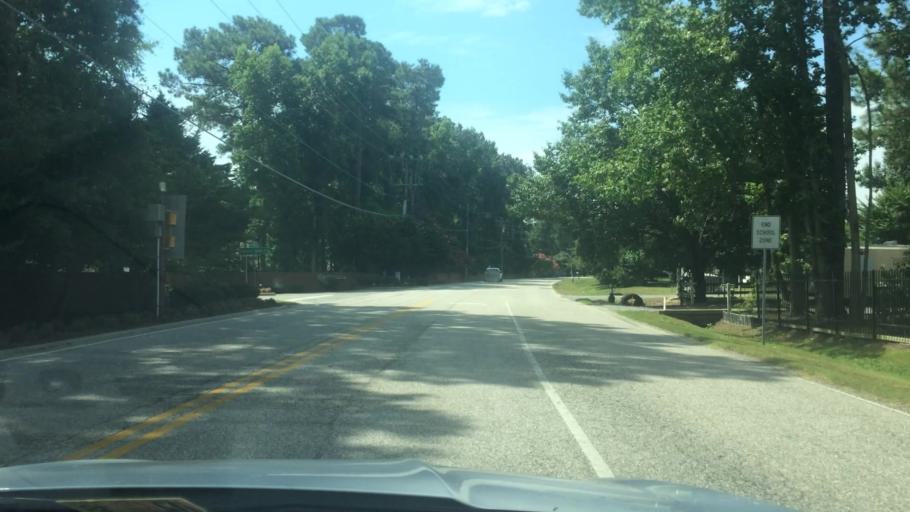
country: US
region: Virginia
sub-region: City of Poquoson
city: Poquoson
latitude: 37.1122
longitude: -76.4295
